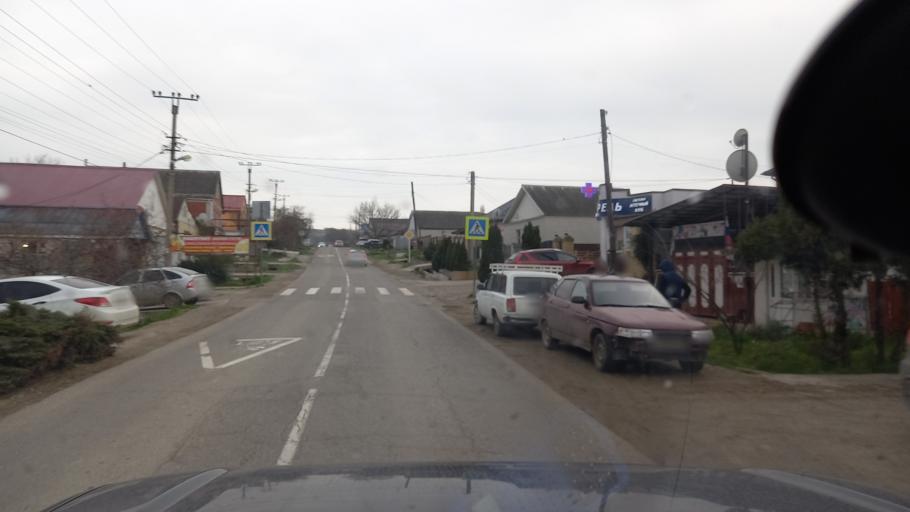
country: RU
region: Krasnodarskiy
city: Sukko
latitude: 44.8533
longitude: 37.4368
